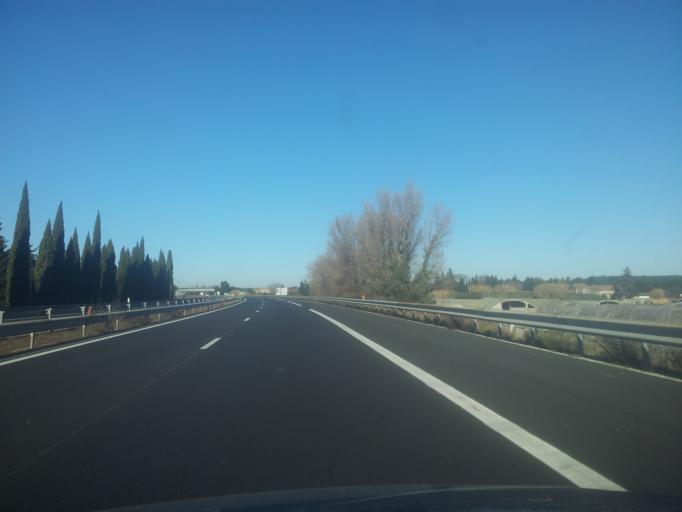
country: FR
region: Provence-Alpes-Cote d'Azur
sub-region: Departement du Vaucluse
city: Caderousse
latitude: 44.1063
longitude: 4.7898
